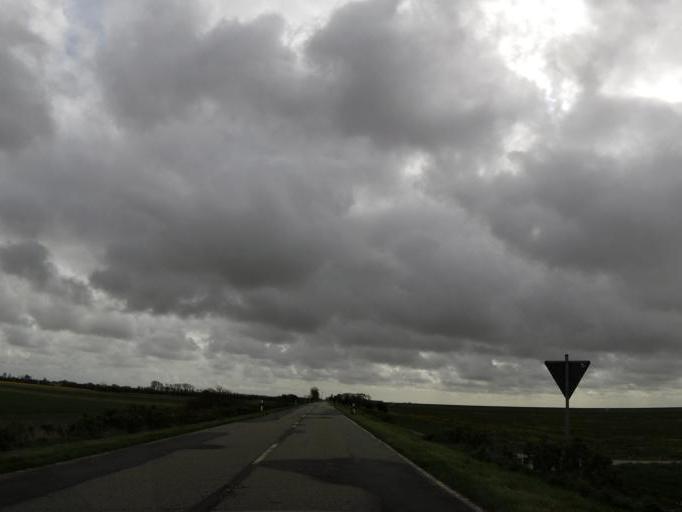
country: DE
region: Schleswig-Holstein
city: Galmsbull
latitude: 54.7498
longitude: 8.7415
